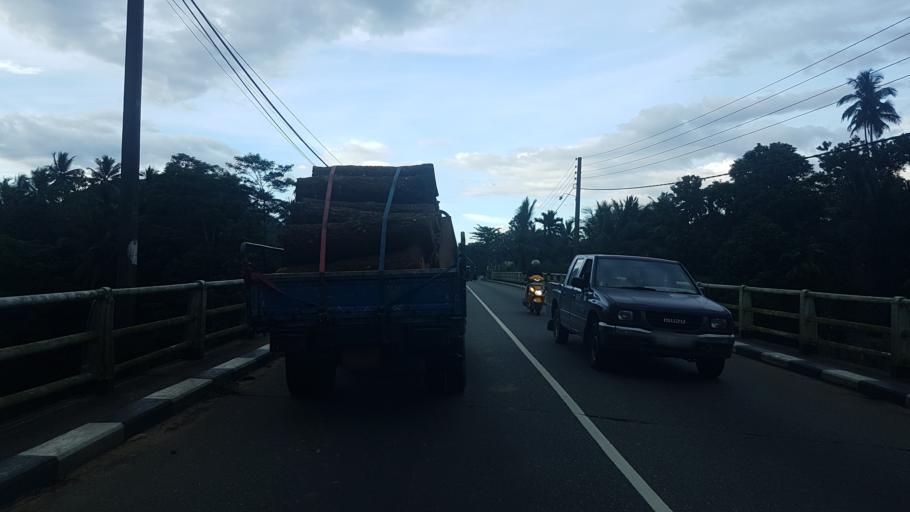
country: LK
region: Western
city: Hanwella Ihala
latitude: 7.0198
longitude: 80.2630
